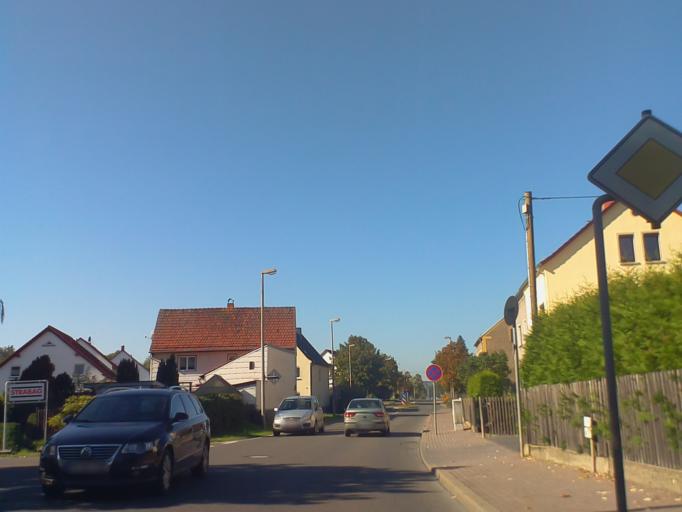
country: DE
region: Thuringia
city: Hartmannsdorf
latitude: 50.8634
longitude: 12.0196
